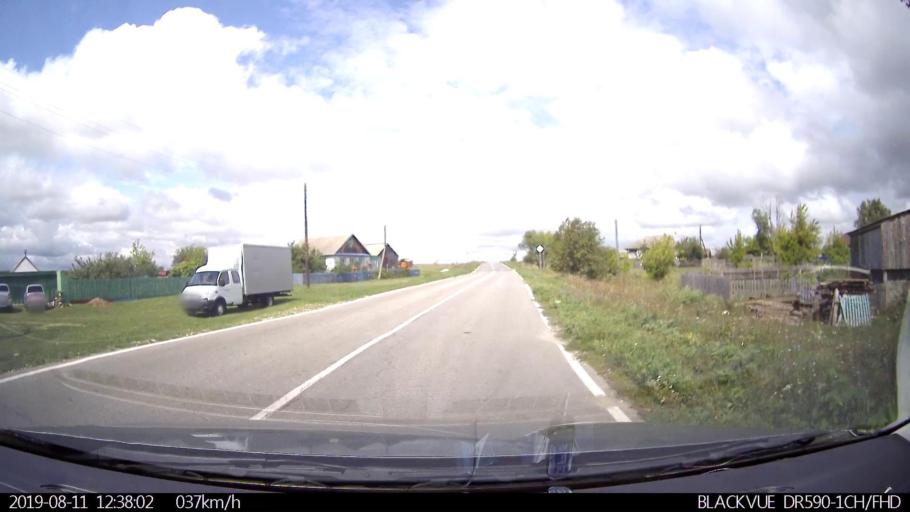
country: RU
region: Ulyanovsk
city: Ignatovka
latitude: 53.8246
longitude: 47.8089
